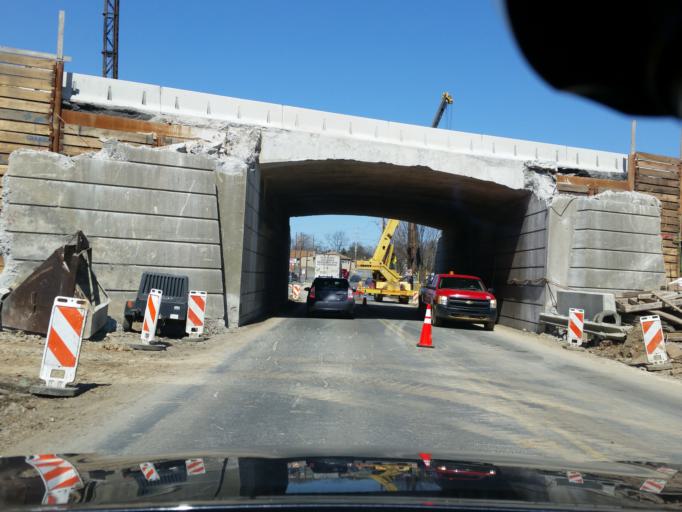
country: US
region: Pennsylvania
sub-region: Cumberland County
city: Carlisle
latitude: 40.2204
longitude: -77.1865
